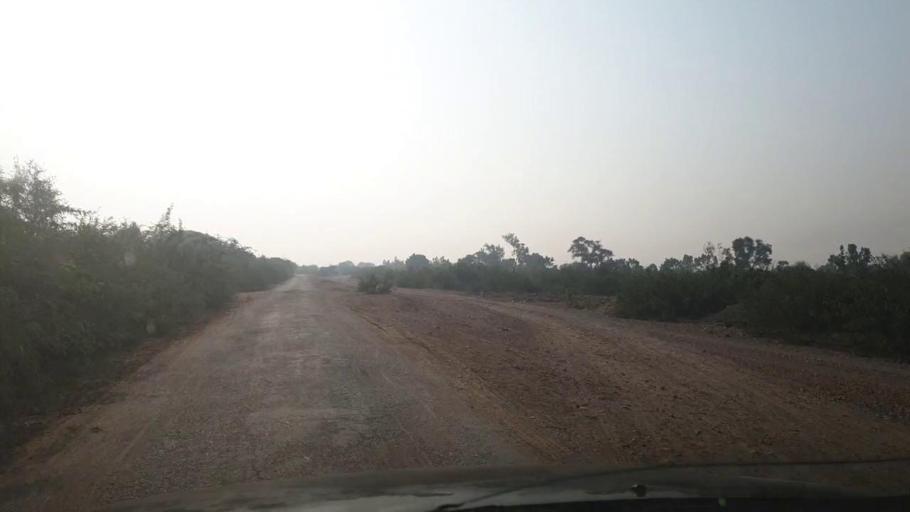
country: PK
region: Sindh
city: Kotri
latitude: 25.3168
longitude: 68.2359
